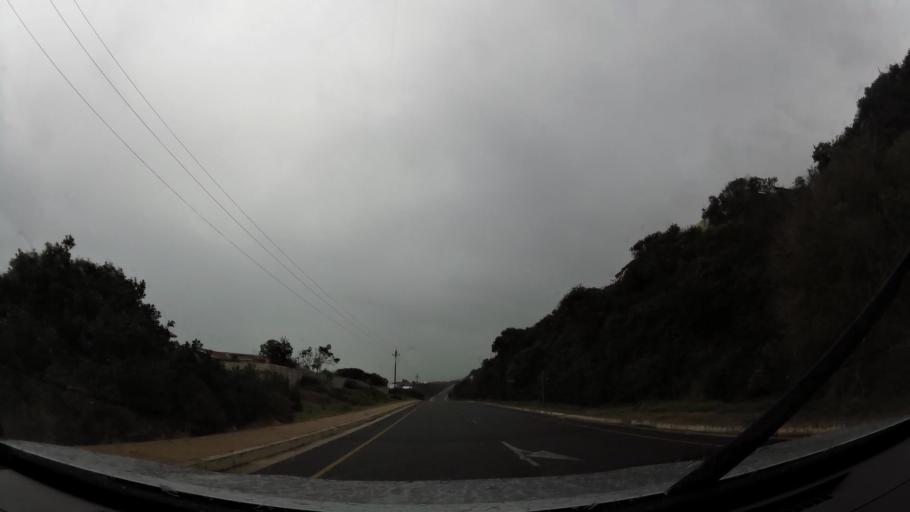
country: ZA
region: Western Cape
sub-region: Eden District Municipality
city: George
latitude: -34.0492
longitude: 22.2875
